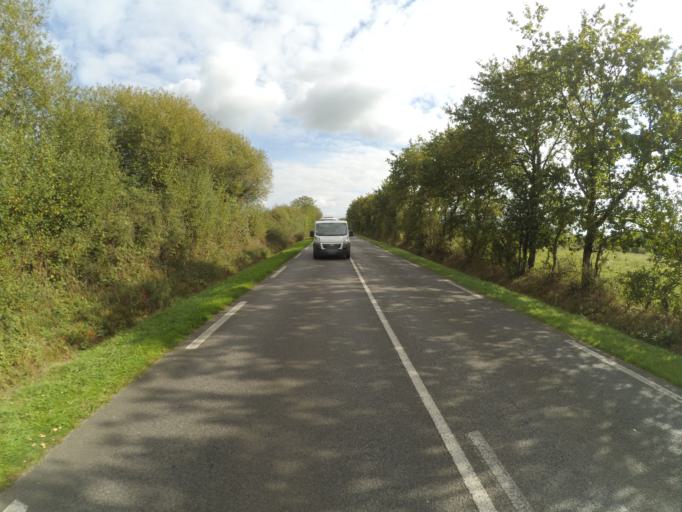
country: FR
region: Pays de la Loire
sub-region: Departement de la Loire-Atlantique
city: Guenrouet
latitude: 47.5416
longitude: -1.9353
